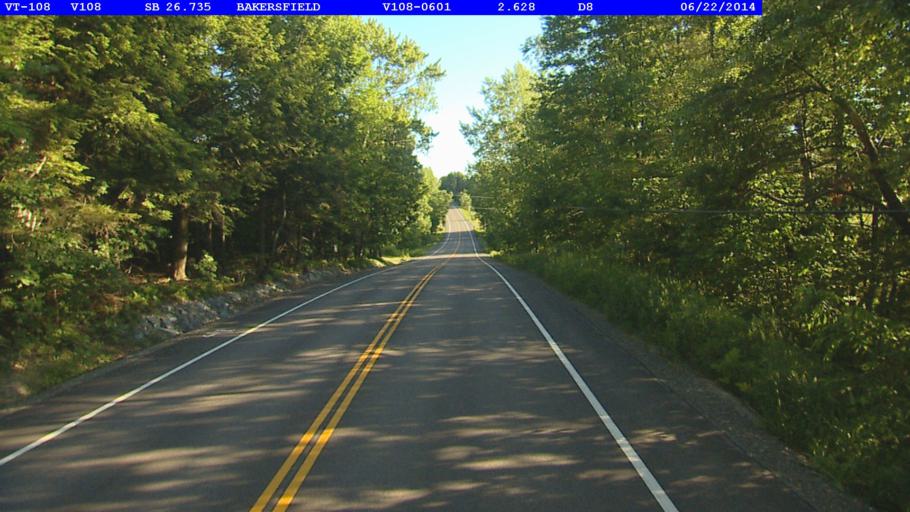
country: US
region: Vermont
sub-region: Franklin County
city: Enosburg Falls
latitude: 44.7693
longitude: -72.8121
